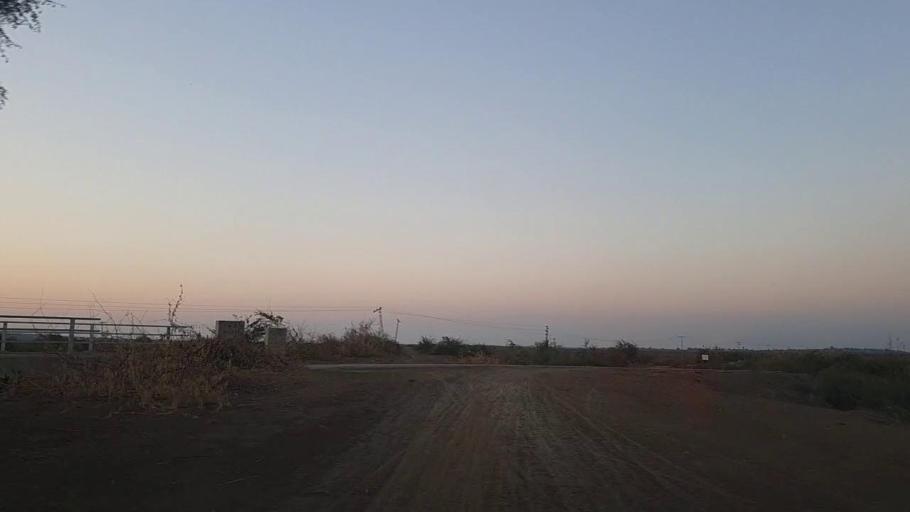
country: PK
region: Sindh
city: Tando Mittha Khan
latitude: 26.0675
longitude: 69.1597
